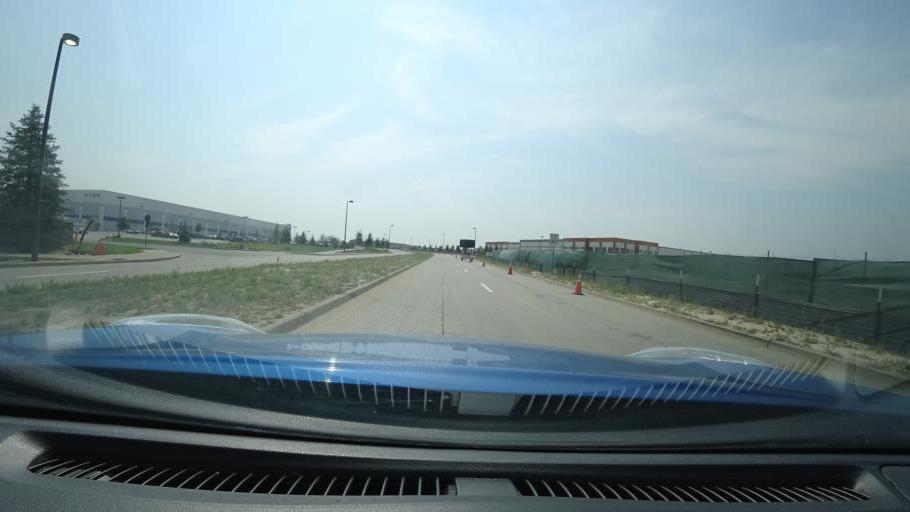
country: US
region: Colorado
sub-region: Adams County
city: Aurora
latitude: 39.7707
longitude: -104.7771
